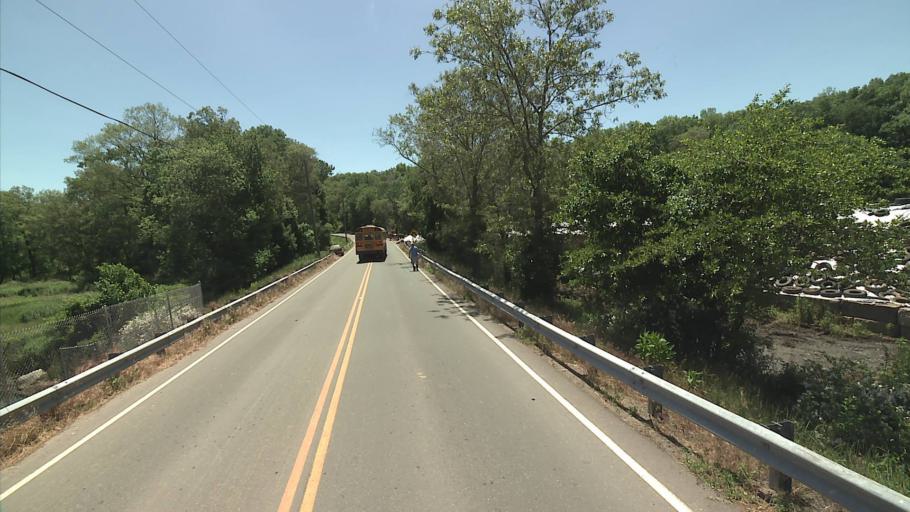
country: US
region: Rhode Island
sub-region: Washington County
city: Hopkinton
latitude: 41.4548
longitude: -71.8137
